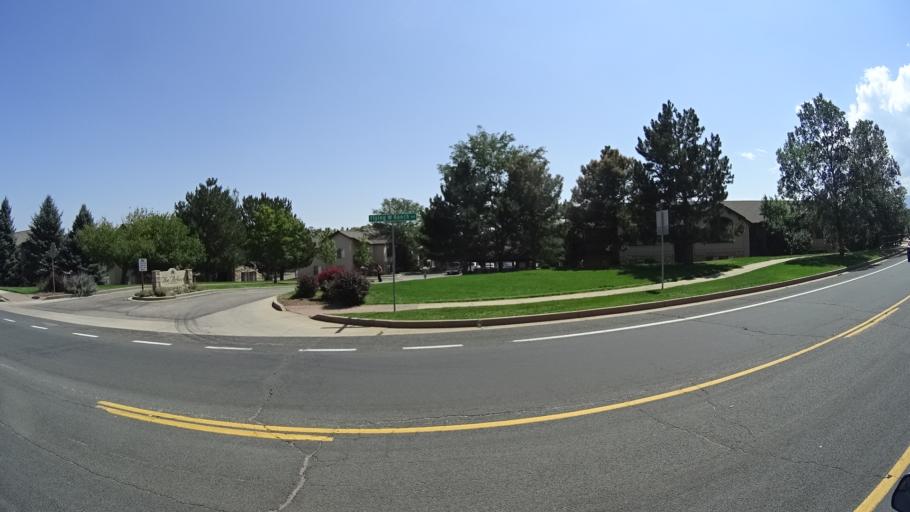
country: US
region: Colorado
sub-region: El Paso County
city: Air Force Academy
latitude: 38.9277
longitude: -104.8661
